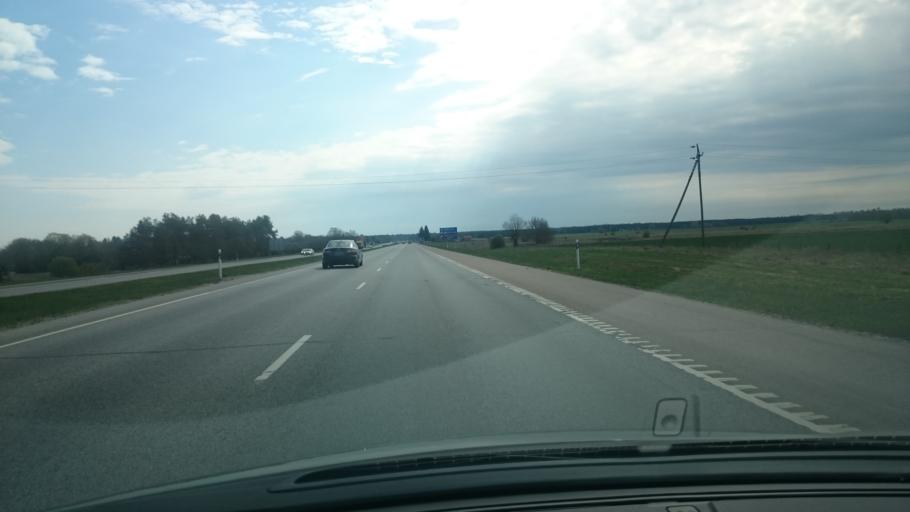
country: EE
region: Harju
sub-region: Raasiku vald
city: Arukula
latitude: 59.4422
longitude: 25.1236
